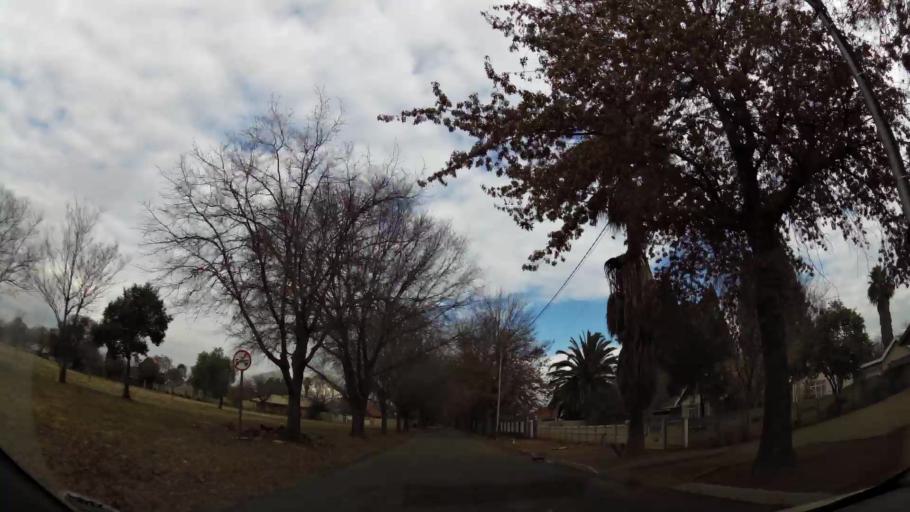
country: ZA
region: Gauteng
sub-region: Sedibeng District Municipality
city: Vereeniging
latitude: -26.6410
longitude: 27.9762
